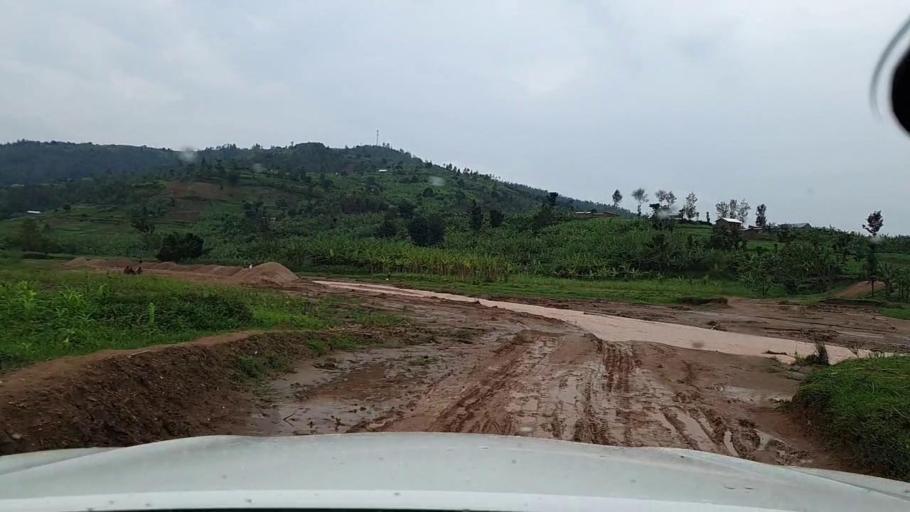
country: RW
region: Kigali
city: Kigali
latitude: -1.8964
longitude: 29.9517
